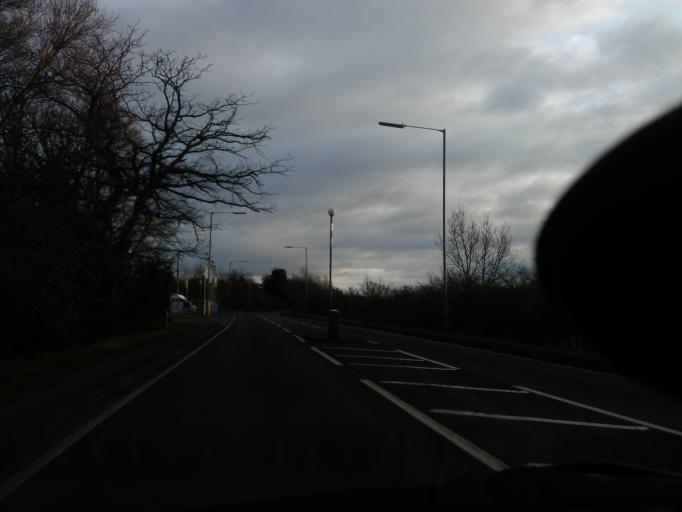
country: GB
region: England
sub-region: Essex
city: Great Bentley
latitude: 51.8701
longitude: 1.0403
